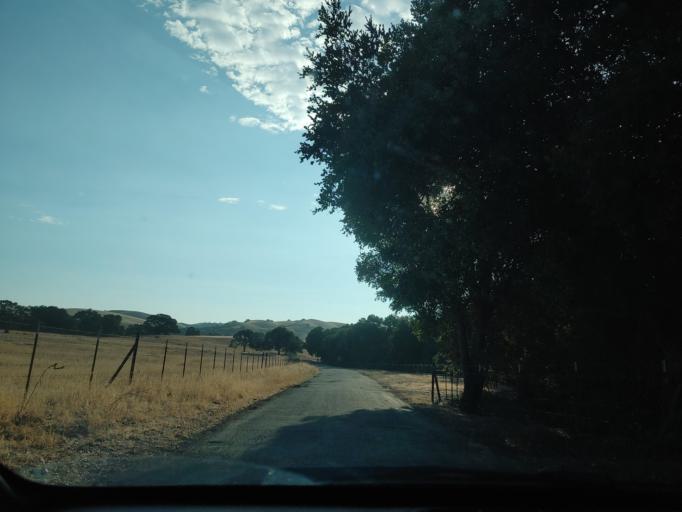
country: US
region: California
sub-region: San Benito County
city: Ridgemark
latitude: 36.7731
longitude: -121.2336
